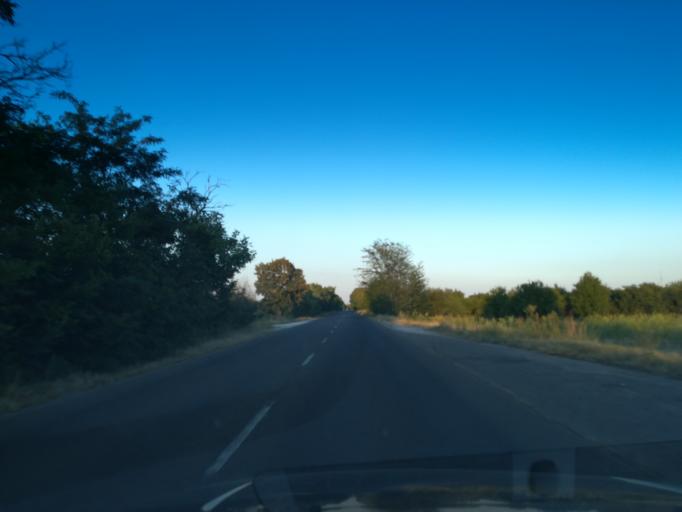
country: BG
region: Plovdiv
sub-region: Obshtina Sadovo
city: Sadovo
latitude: 42.1353
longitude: 25.0016
